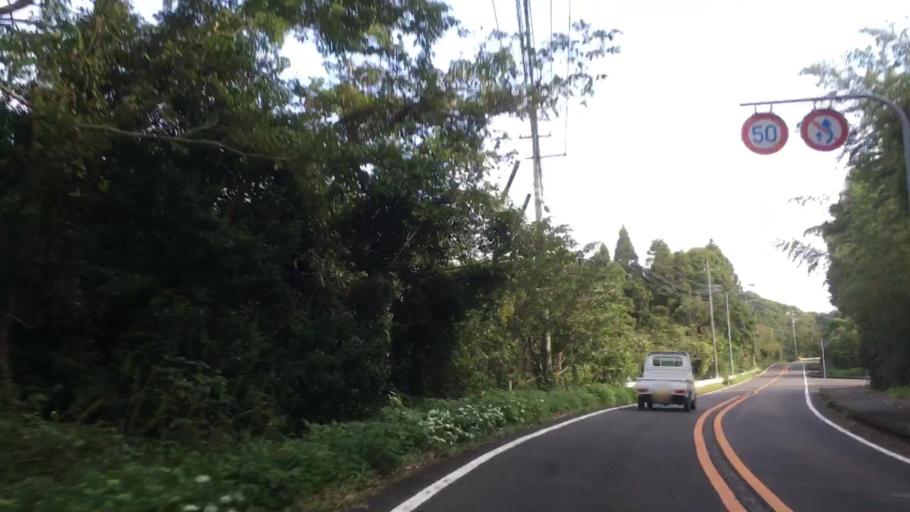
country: JP
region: Nagasaki
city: Sasebo
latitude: 33.0291
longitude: 129.6545
